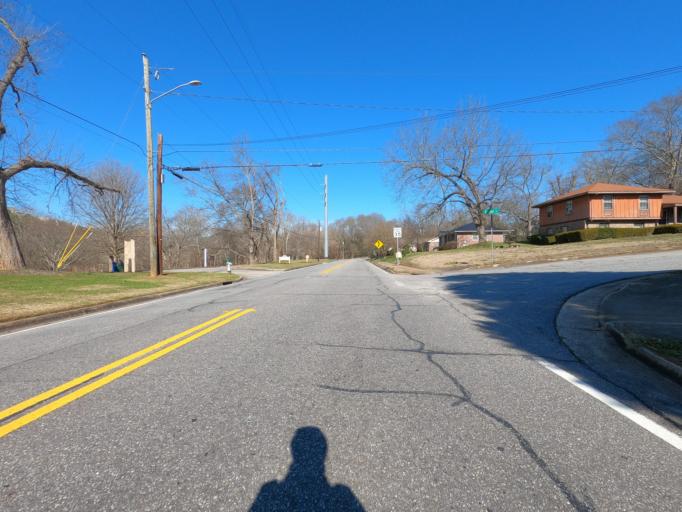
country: US
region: Georgia
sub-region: Clarke County
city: Athens
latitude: 33.9621
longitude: -83.3683
